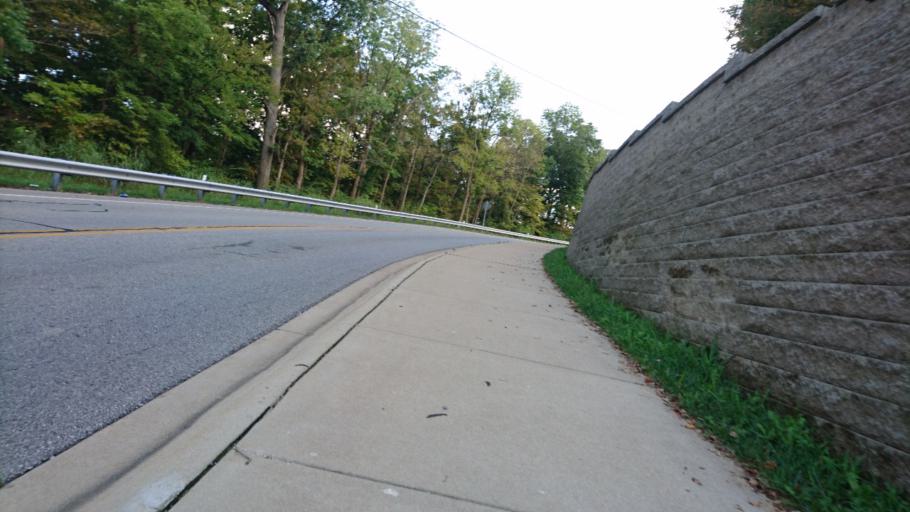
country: US
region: Missouri
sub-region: Saint Louis County
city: Eureka
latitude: 38.5139
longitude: -90.6327
